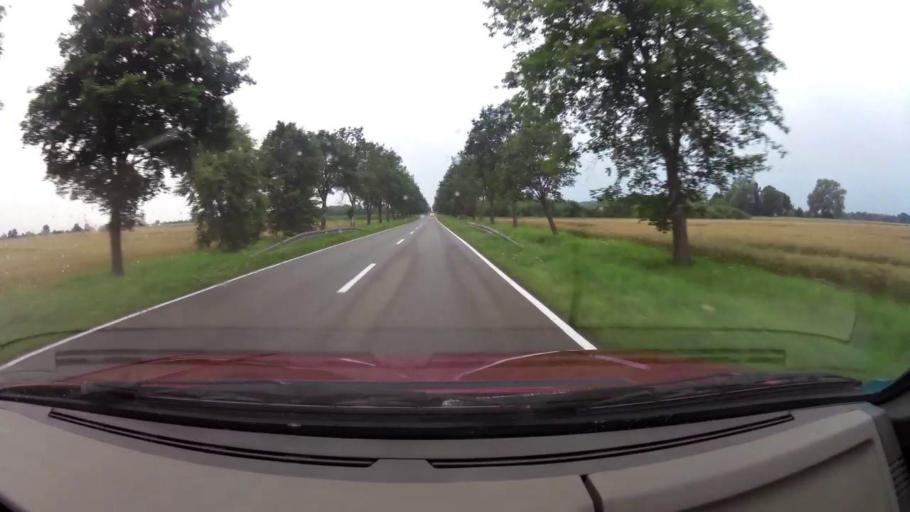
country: PL
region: West Pomeranian Voivodeship
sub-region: Powiat stargardzki
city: Stara Dabrowa
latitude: 53.3873
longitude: 15.1834
